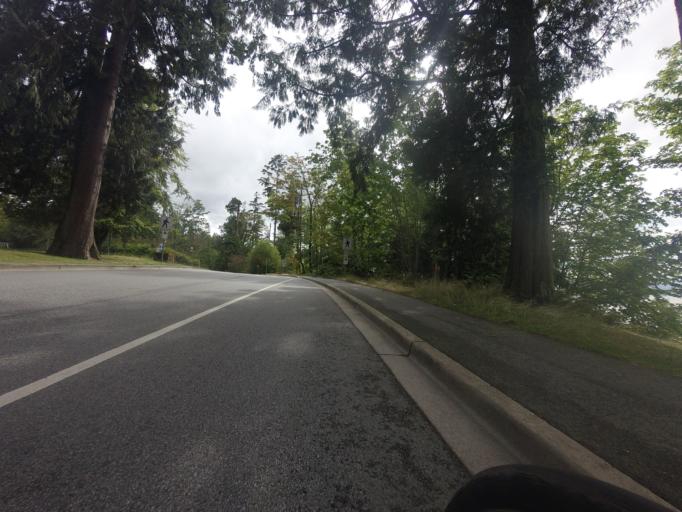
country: CA
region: British Columbia
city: West End
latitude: 49.3108
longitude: -123.1489
